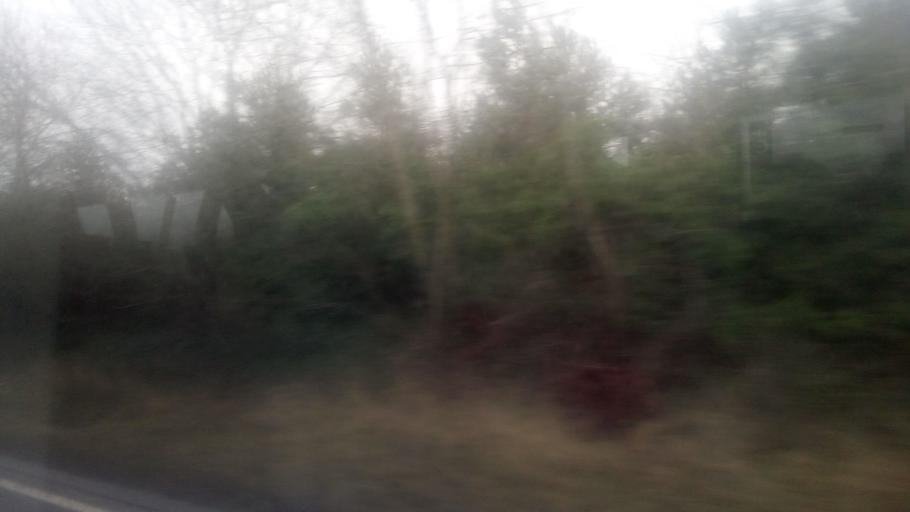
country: GB
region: Scotland
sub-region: The Scottish Borders
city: Newtown St Boswells
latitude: 55.5888
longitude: -2.6723
